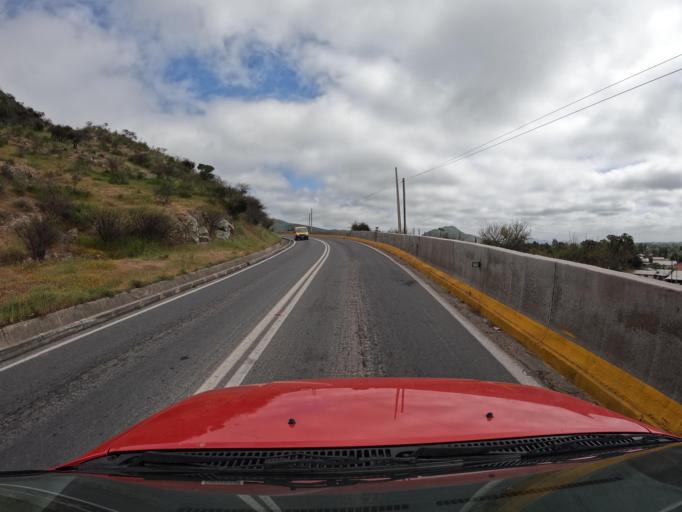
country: CL
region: O'Higgins
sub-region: Provincia de Colchagua
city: Santa Cruz
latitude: -34.6617
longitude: -71.4125
